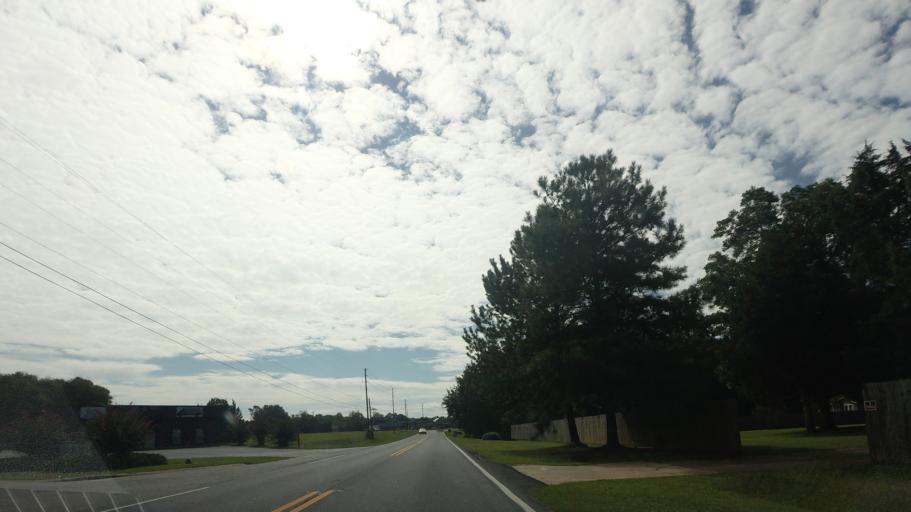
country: US
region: Georgia
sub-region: Houston County
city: Centerville
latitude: 32.6447
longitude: -83.6918
